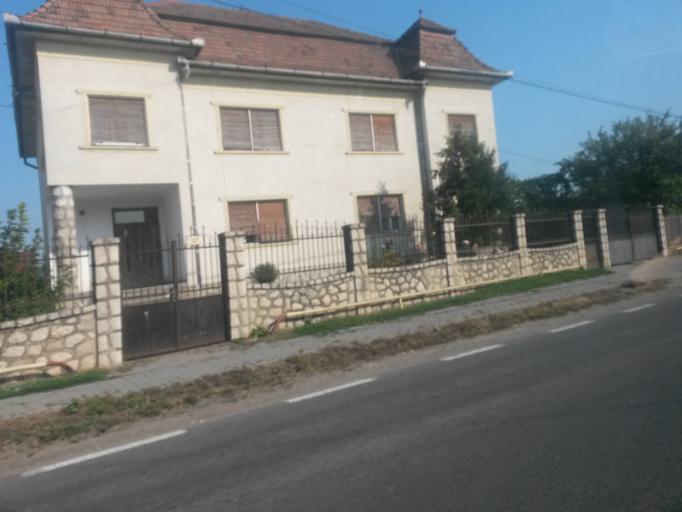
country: RO
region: Alba
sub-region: Comuna Unirea
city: Unirea
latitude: 46.3999
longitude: 23.8093
